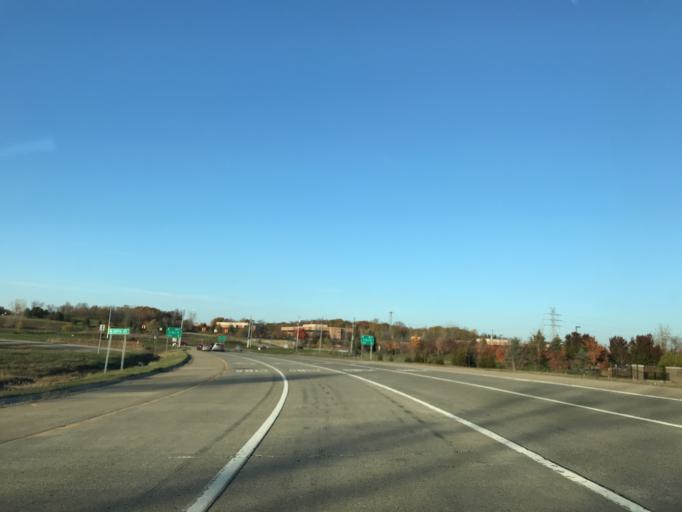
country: US
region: Michigan
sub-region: Oakland County
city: Novi
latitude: 42.4948
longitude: -83.4443
